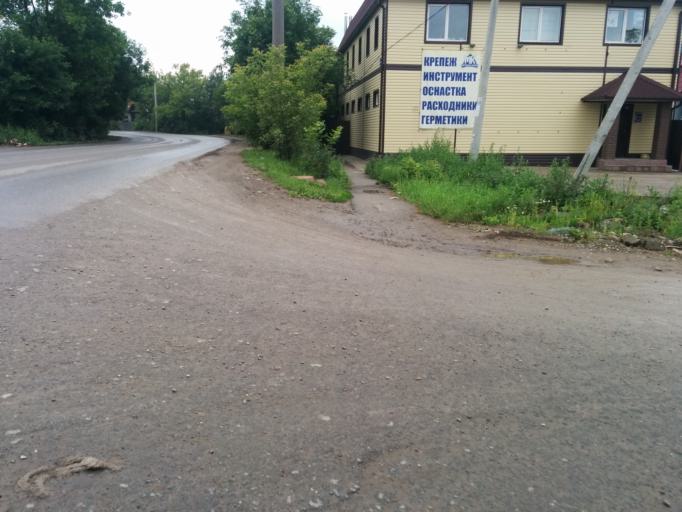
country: RU
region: Perm
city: Perm
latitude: 57.9865
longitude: 56.3042
